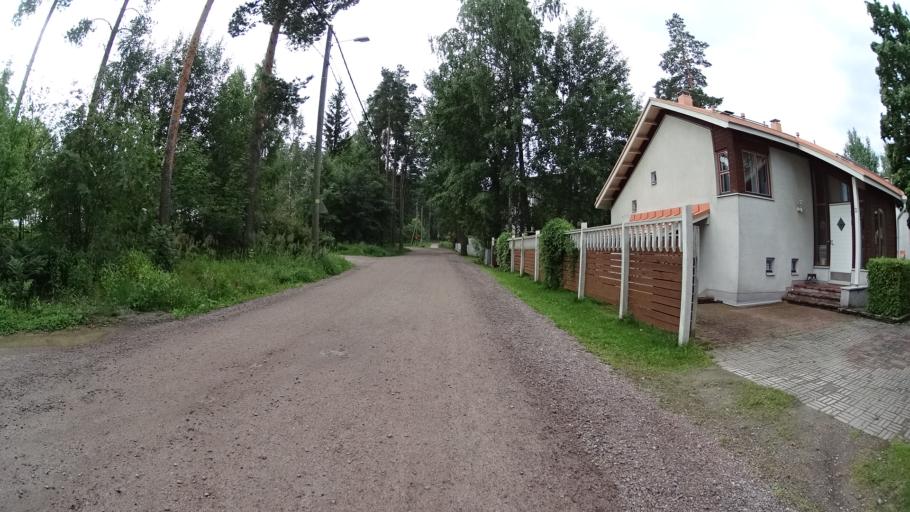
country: FI
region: Uusimaa
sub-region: Helsinki
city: Kilo
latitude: 60.2317
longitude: 24.8063
